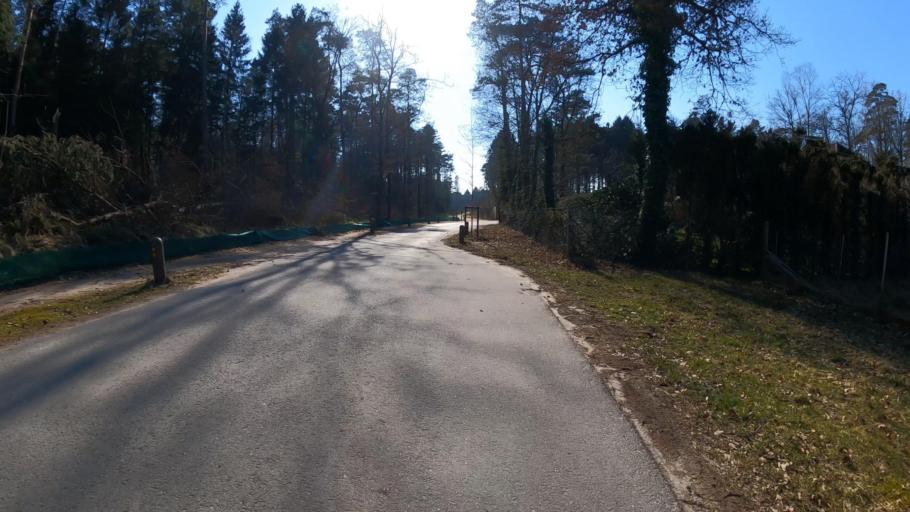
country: DE
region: Lower Saxony
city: Buchholz in der Nordheide
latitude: 53.3151
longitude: 9.8528
